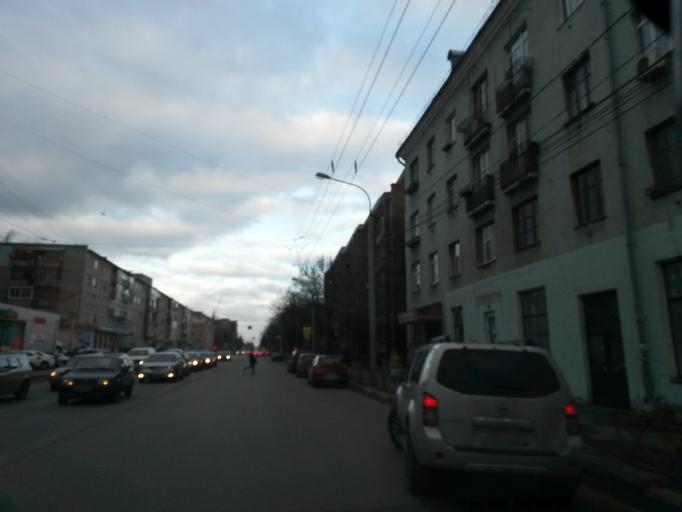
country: RU
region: Jaroslavl
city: Yaroslavl
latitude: 57.6205
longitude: 39.8539
